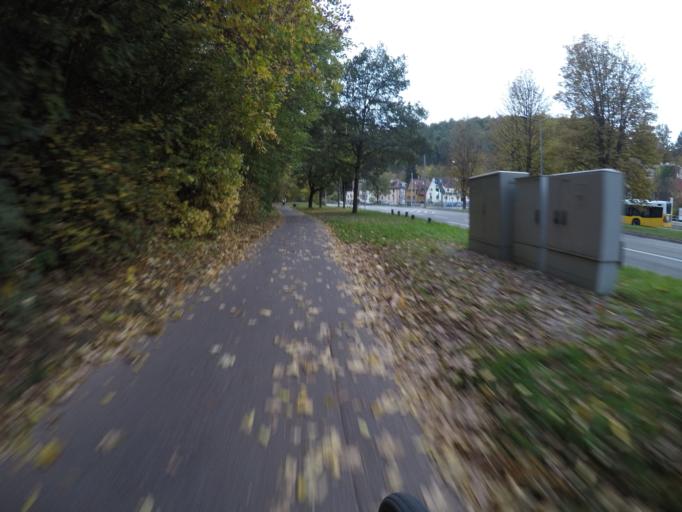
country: DE
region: Baden-Wuerttemberg
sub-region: Regierungsbezirk Stuttgart
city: Stuttgart
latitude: 48.7536
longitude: 9.1391
